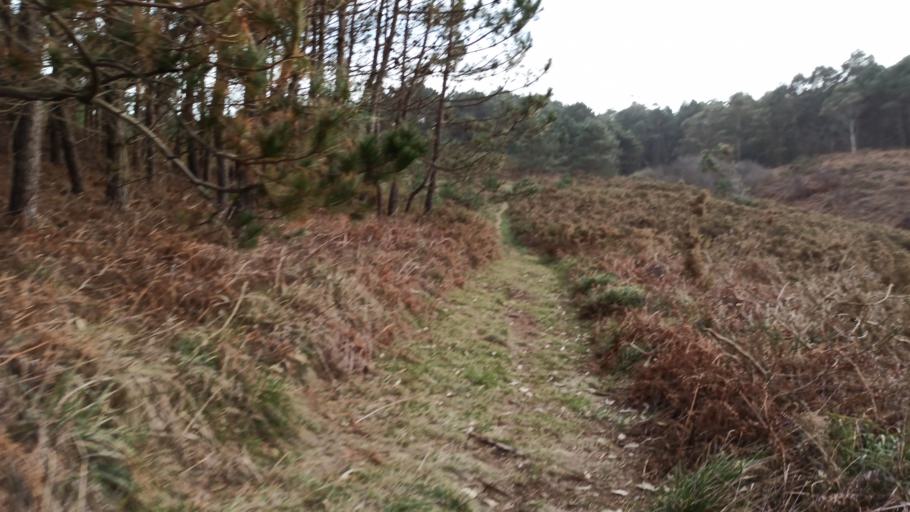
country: ES
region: Galicia
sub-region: Provincia da Coruna
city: A Coruna
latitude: 43.3983
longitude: -8.3352
